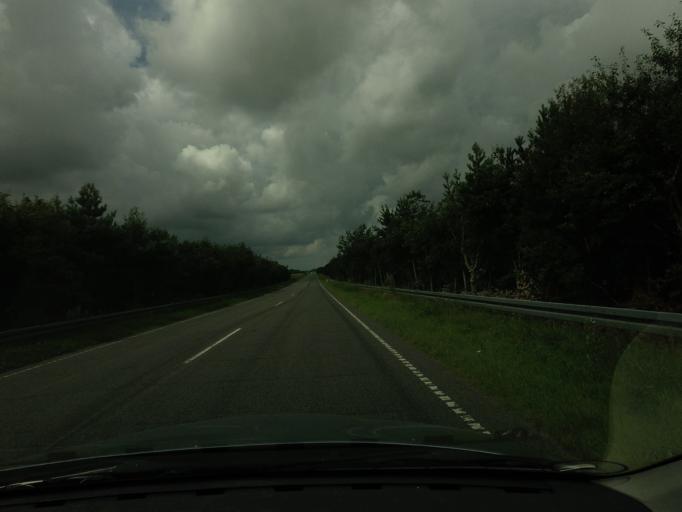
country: DK
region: North Denmark
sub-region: Hjorring Kommune
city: Hjorring
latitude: 57.4233
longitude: 10.0243
